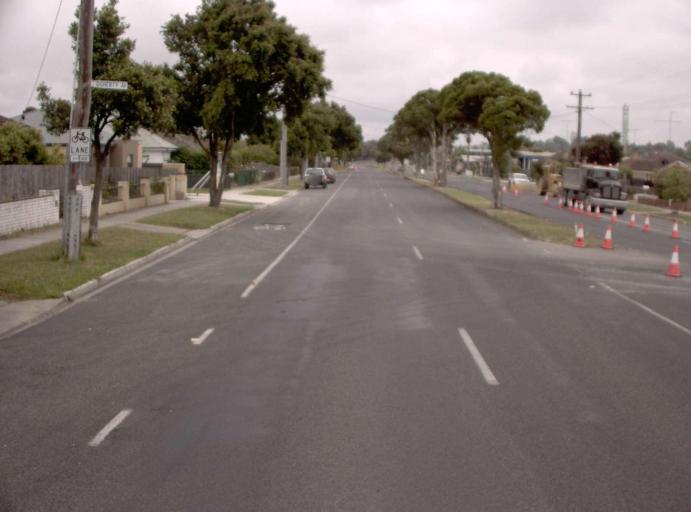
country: AU
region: Victoria
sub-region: Latrobe
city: Morwell
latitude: -38.2372
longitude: 146.4052
